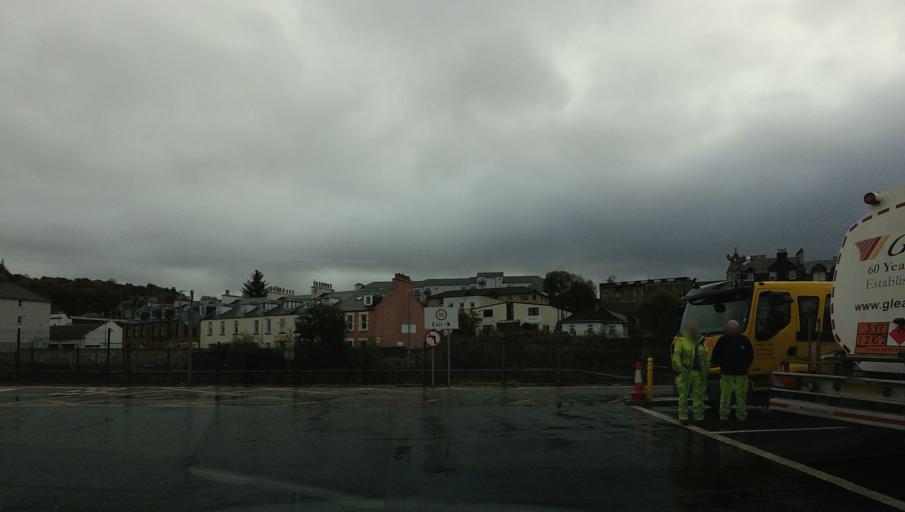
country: GB
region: Scotland
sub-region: Argyll and Bute
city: Oban
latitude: 56.4111
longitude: -5.4773
